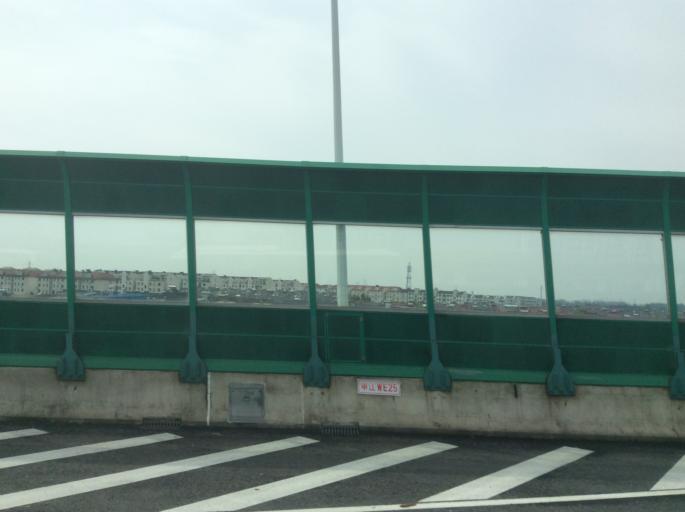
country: CN
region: Shanghai Shi
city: Kangqiao
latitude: 31.1868
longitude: 121.6225
